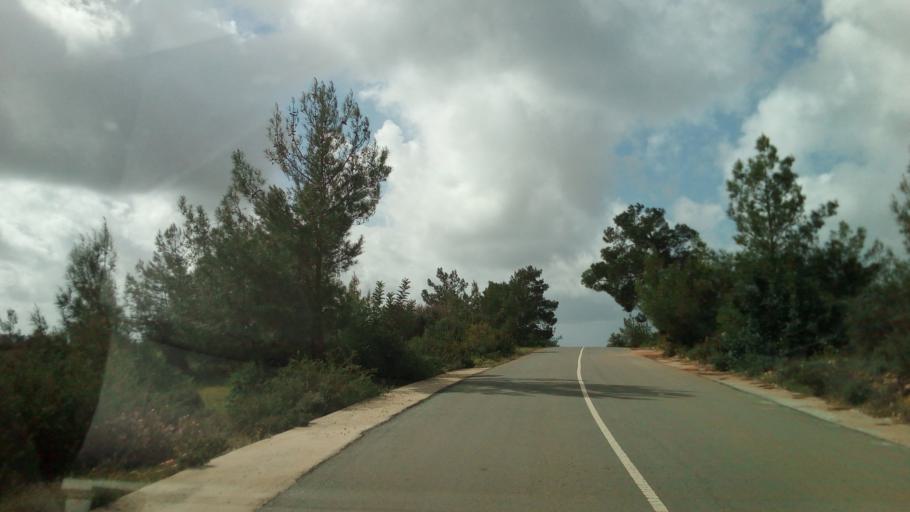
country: CY
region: Limassol
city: Sotira
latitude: 34.7282
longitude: 32.8659
